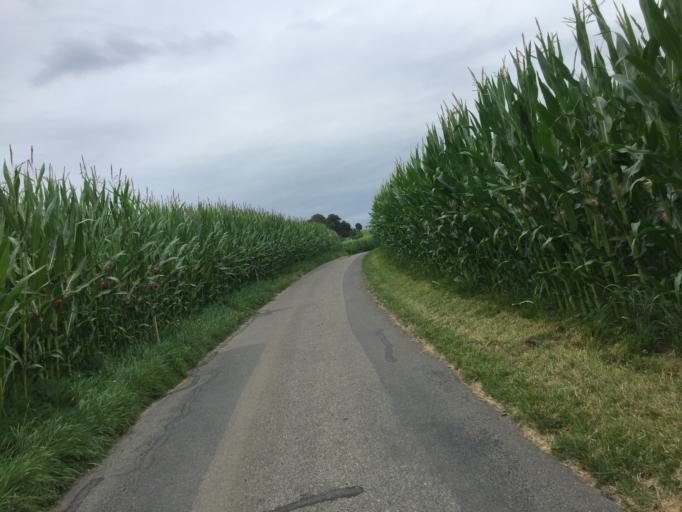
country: CH
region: Bern
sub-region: Bern-Mittelland District
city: Biglen
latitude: 46.9156
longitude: 7.5953
